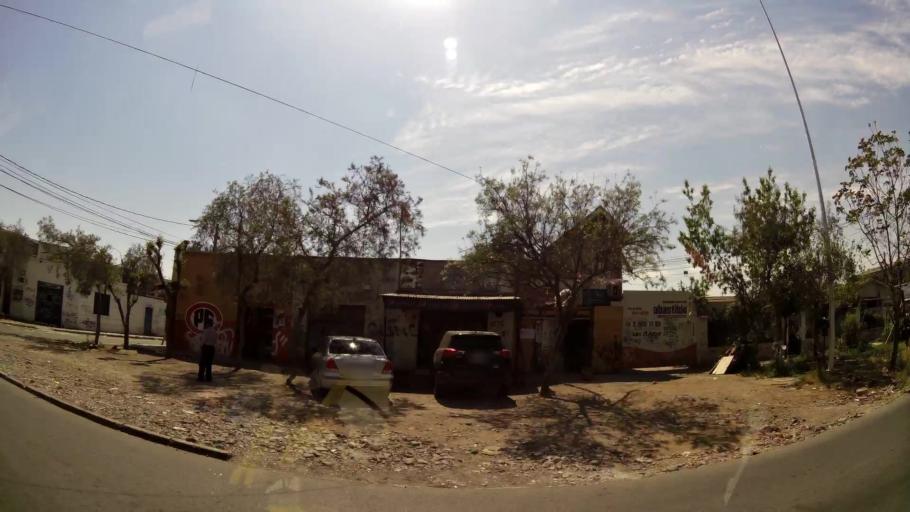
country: CL
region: Santiago Metropolitan
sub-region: Provincia de Santiago
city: La Pintana
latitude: -33.5446
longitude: -70.6537
